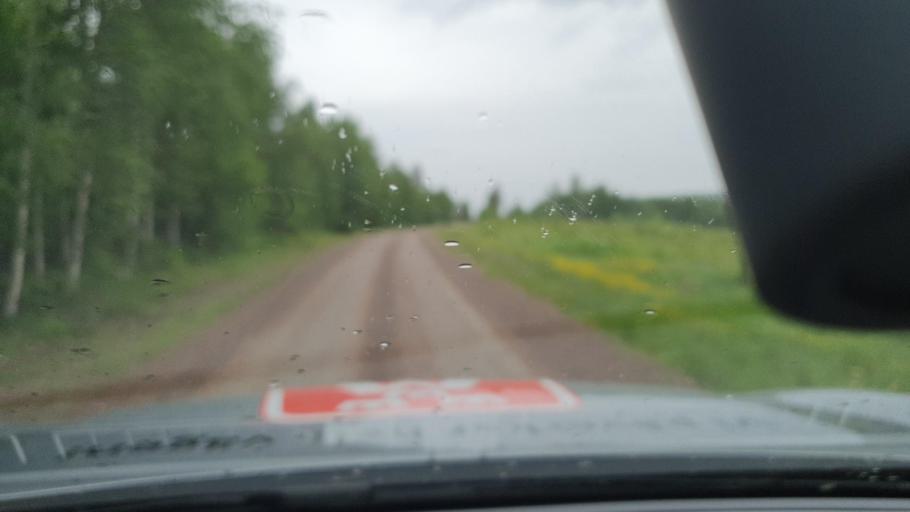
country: SE
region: Norrbotten
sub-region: Overkalix Kommun
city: OEverkalix
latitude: 66.5090
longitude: 22.7486
